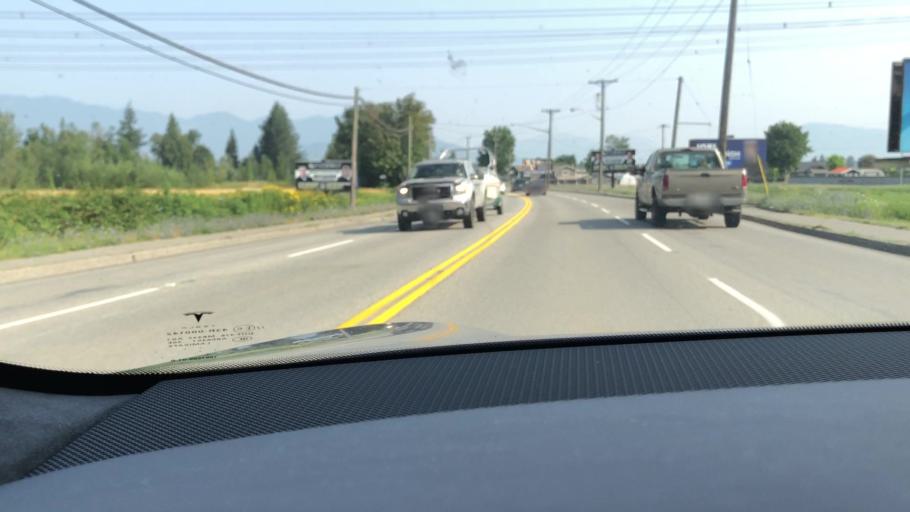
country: CA
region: British Columbia
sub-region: Fraser Valley Regional District
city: Chilliwack
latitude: 49.1145
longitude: -121.9574
